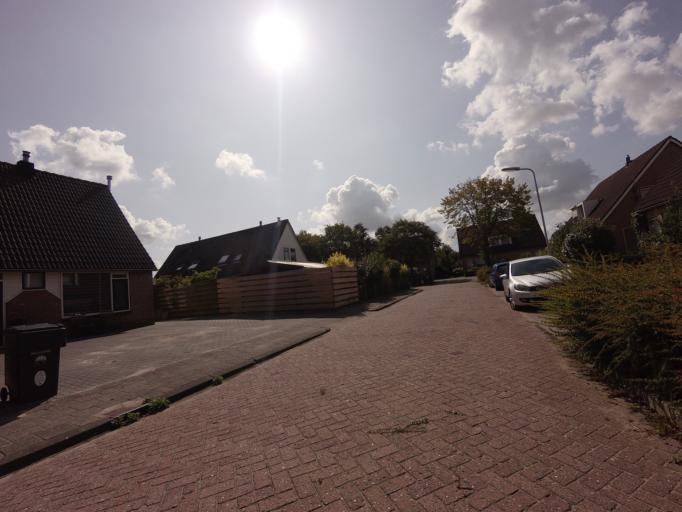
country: NL
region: Friesland
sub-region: Gemeente Het Bildt
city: Sint Annaparochie
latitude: 53.2807
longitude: 5.6650
